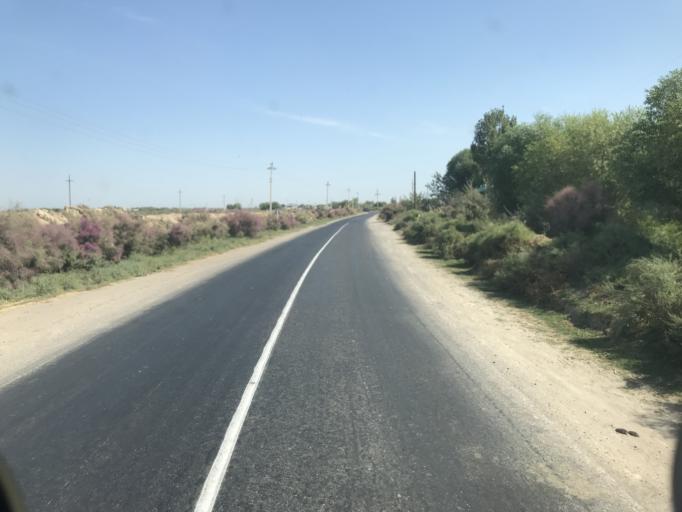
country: KZ
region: Ongtustik Qazaqstan
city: Myrzakent
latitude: 40.7253
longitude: 68.5348
